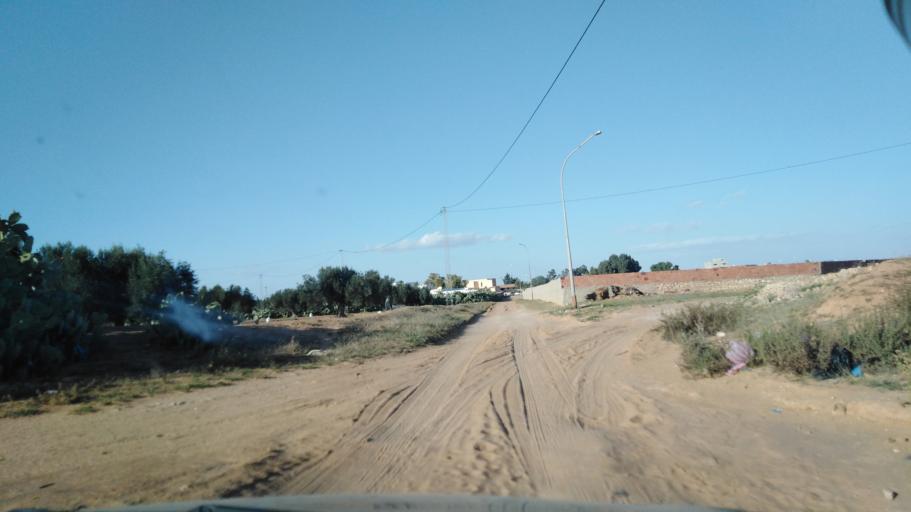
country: TN
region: Al Mahdiyah
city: Shurban
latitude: 34.9572
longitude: 10.3631
